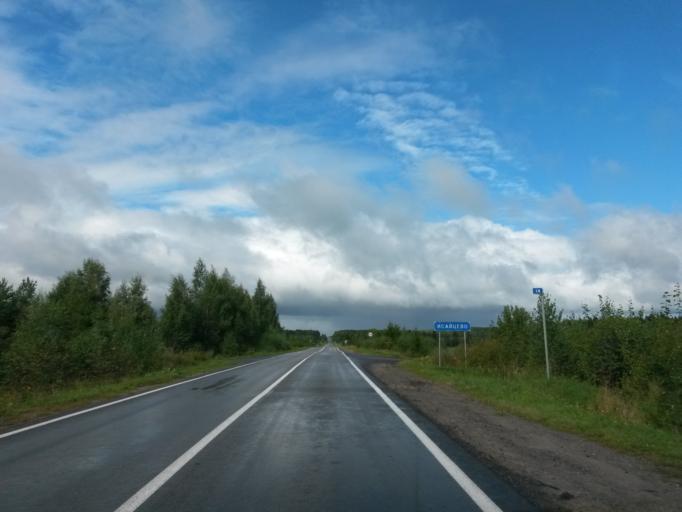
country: RU
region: Jaroslavl
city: Konstantinovskiy
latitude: 57.8090
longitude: 39.7383
